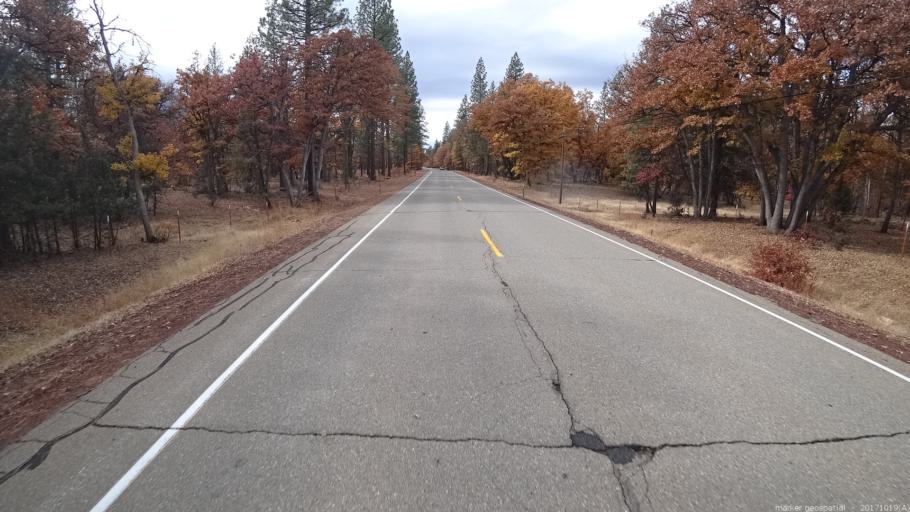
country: US
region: California
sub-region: Shasta County
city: Burney
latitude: 41.0945
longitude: -121.5272
